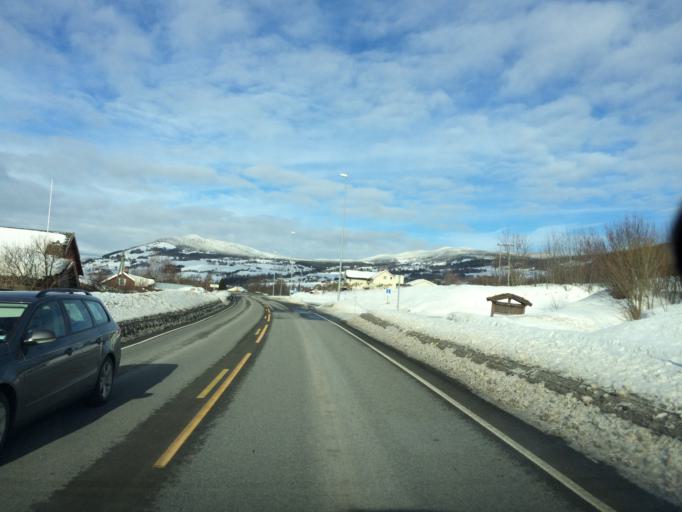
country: NO
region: Oppland
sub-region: Gausdal
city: Segalstad bru
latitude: 61.2014
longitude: 10.3048
